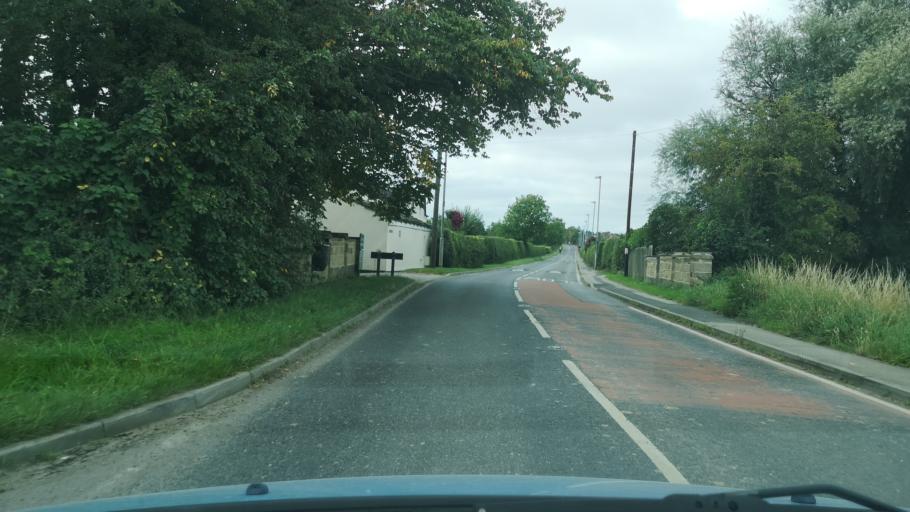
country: GB
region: England
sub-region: City and Borough of Wakefield
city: Badsworth
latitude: 53.6365
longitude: -1.2838
